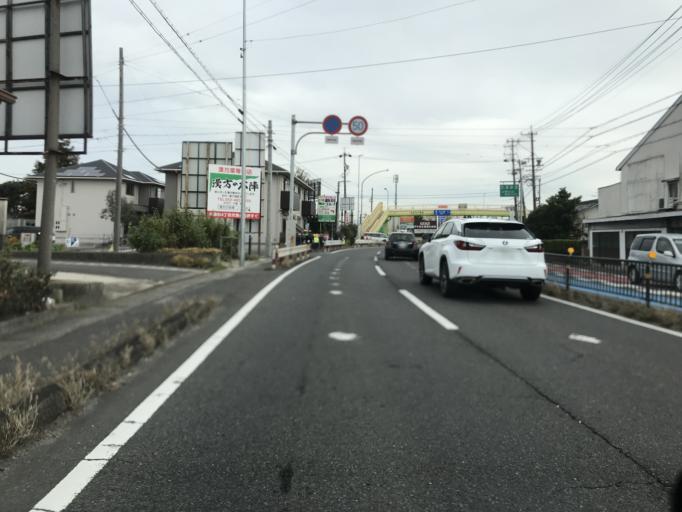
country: JP
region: Aichi
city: Kanie
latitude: 35.1840
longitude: 136.8390
